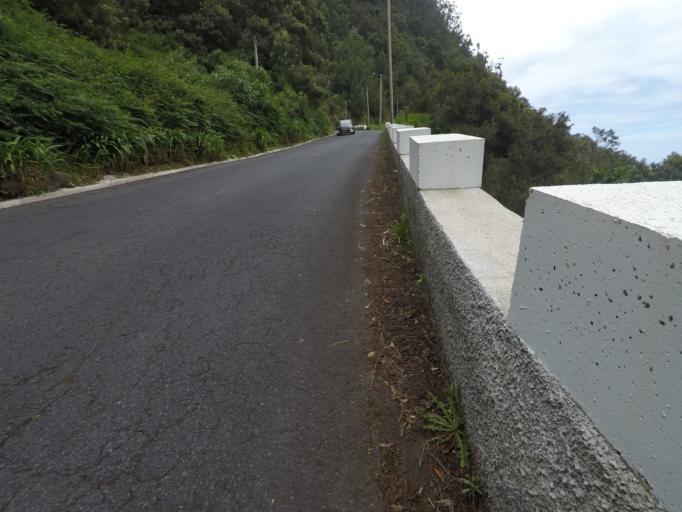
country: PT
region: Madeira
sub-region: Santana
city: Santana
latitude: 32.7914
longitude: -16.8630
